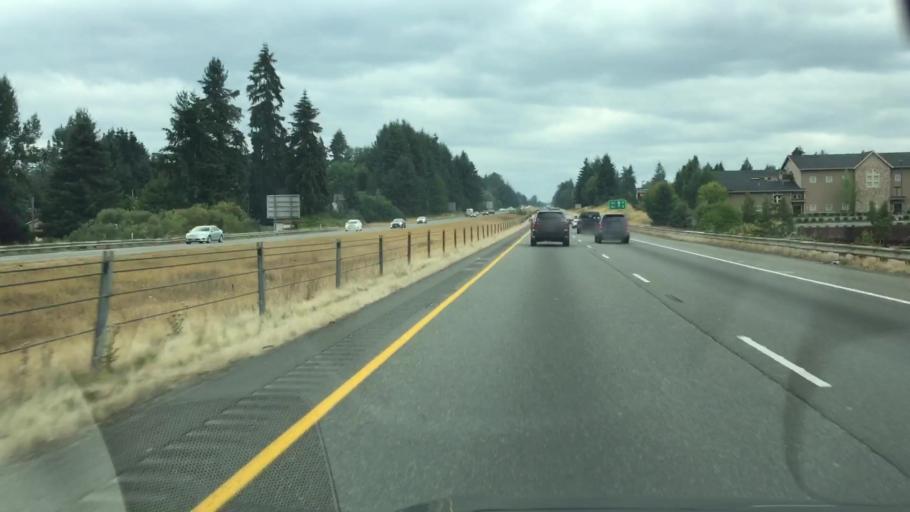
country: US
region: Washington
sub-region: Pierce County
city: Puyallup
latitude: 47.1588
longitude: -122.3171
